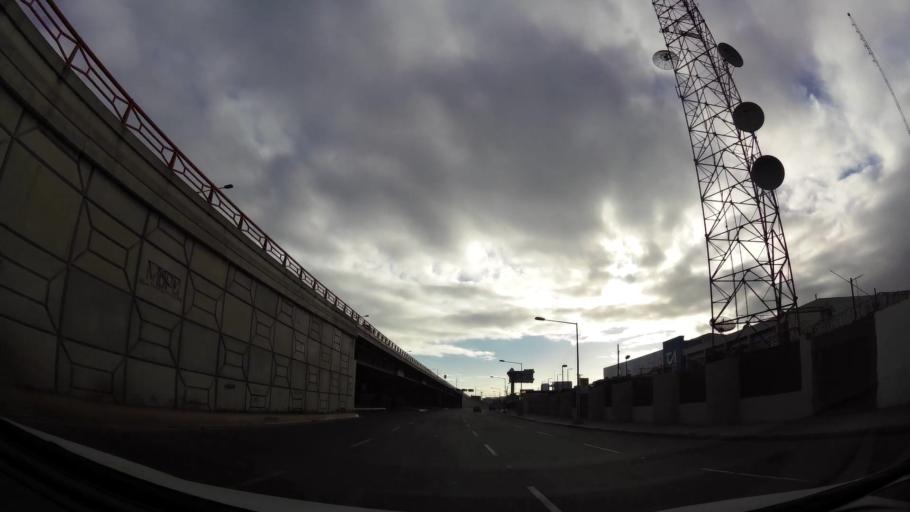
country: DO
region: Nacional
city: La Julia
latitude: 18.4813
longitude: -69.9558
